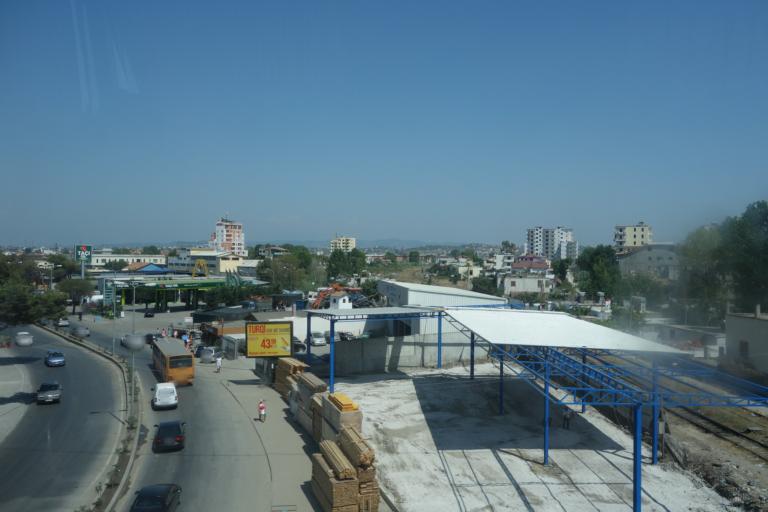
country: AL
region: Durres
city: Durres
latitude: 41.3171
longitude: 19.4704
